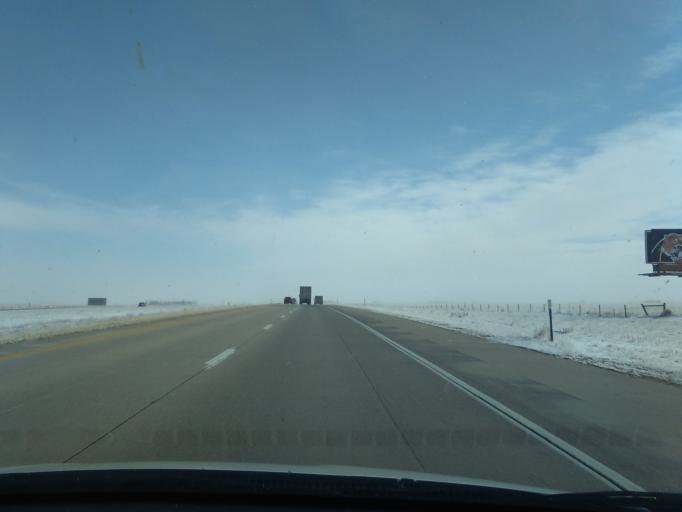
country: US
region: Wyoming
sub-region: Laramie County
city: Fox Farm-College
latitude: 41.1563
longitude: -104.4465
